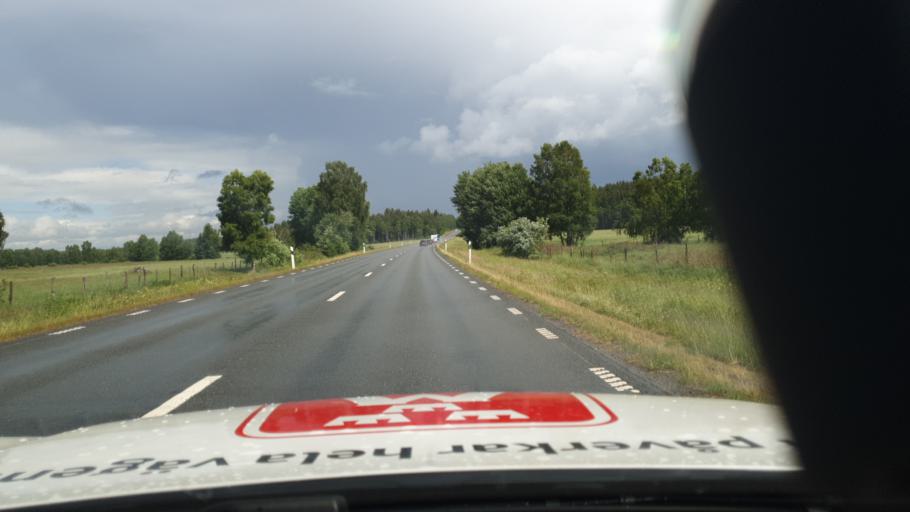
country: SE
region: Vaestra Goetaland
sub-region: Tidaholms Kommun
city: Tidaholm
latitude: 58.1334
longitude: 13.8752
